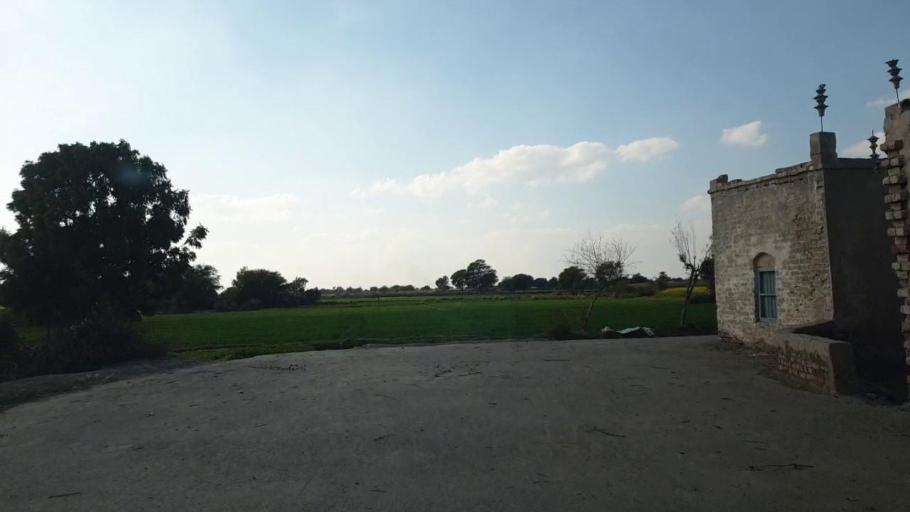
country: PK
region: Sindh
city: Shahpur Chakar
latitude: 26.1047
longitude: 68.5895
